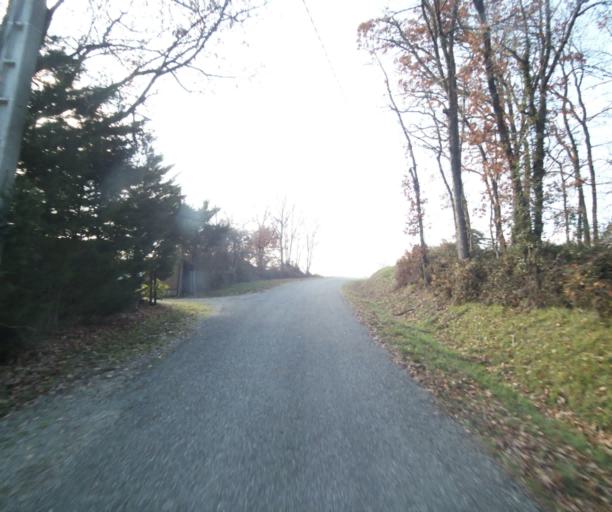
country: FR
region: Midi-Pyrenees
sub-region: Departement du Tarn-et-Garonne
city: Saint-Nicolas-de-la-Grave
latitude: 44.1236
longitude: 1.0350
